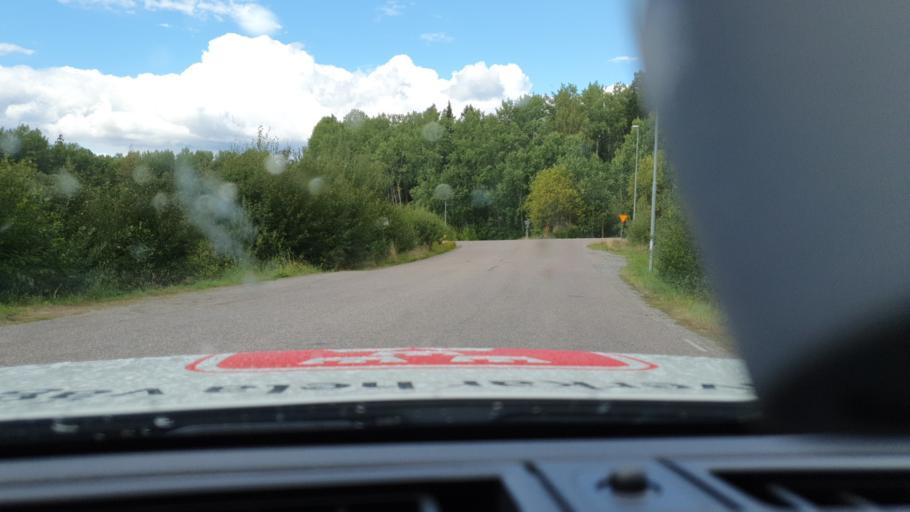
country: SE
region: Stockholm
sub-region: Vaxholms Kommun
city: Vaxholm
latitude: 59.3928
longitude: 18.4129
